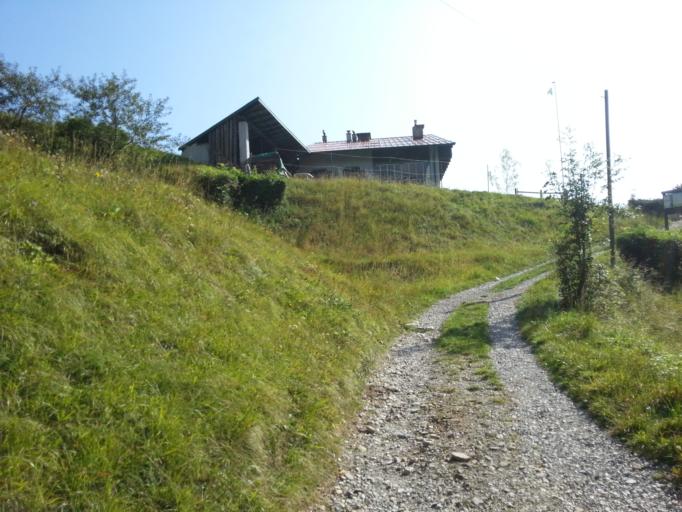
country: IT
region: Lombardy
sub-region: Provincia di Lecco
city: Pasturo
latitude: 45.9370
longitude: 9.4376
